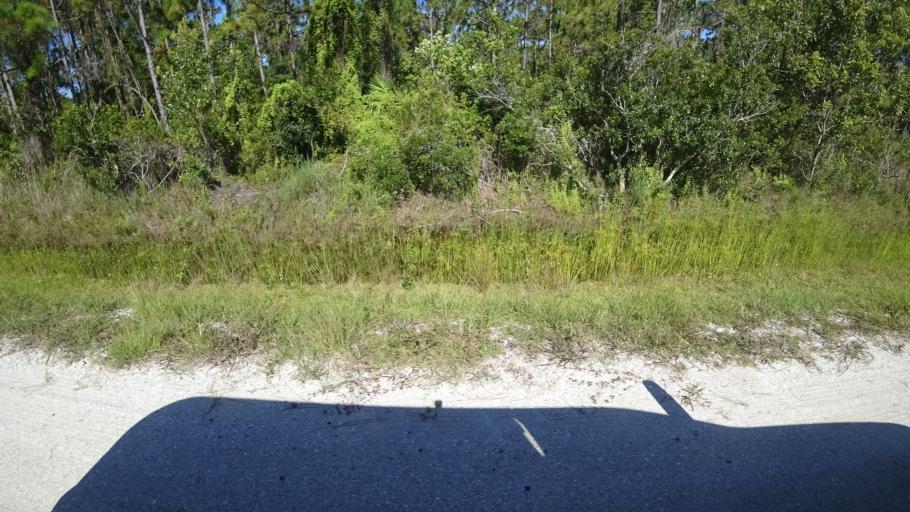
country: US
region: Florida
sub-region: Sarasota County
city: The Meadows
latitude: 27.4138
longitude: -82.2915
